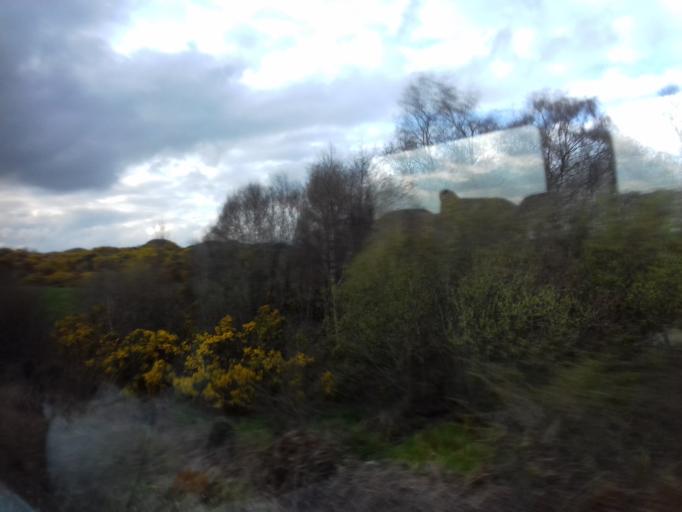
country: IE
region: Leinster
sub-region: An Iarmhi
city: Rathwire
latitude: 53.4869
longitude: -7.1144
